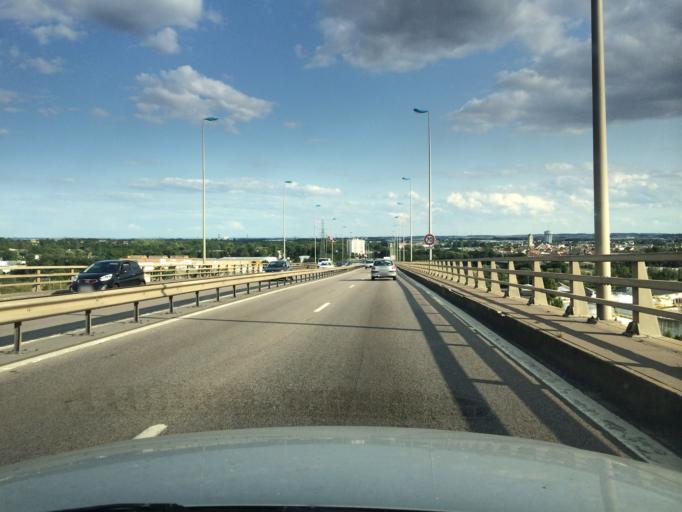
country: FR
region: Lower Normandy
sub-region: Departement du Calvados
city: Mondeville
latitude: 49.1852
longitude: -0.3286
